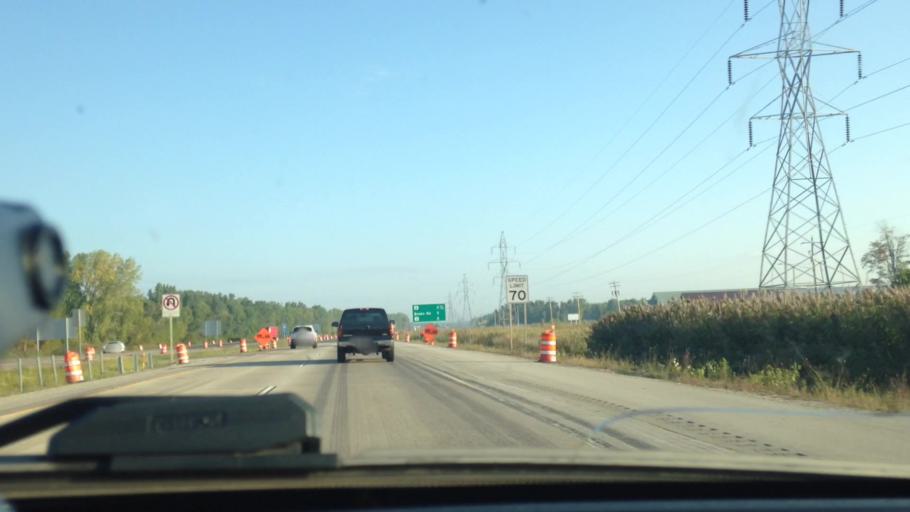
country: US
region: Wisconsin
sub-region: Brown County
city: Suamico
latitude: 44.5988
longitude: -88.0497
